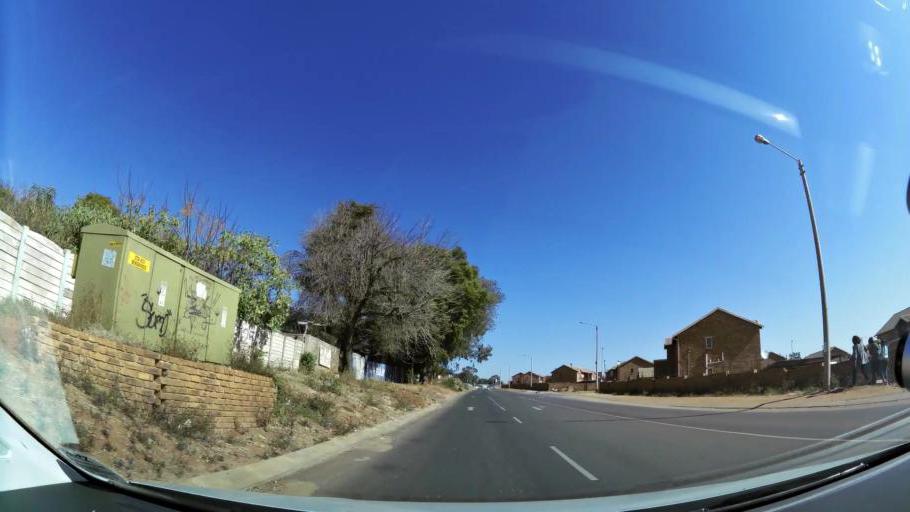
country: ZA
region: Gauteng
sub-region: City of Johannesburg Metropolitan Municipality
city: Modderfontein
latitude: -26.0736
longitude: 28.1916
